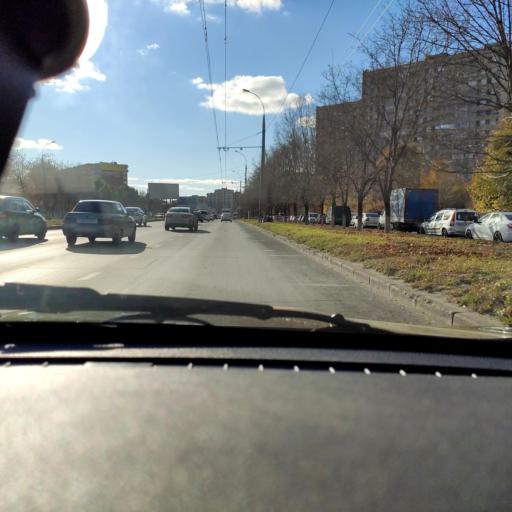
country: RU
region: Samara
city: Tol'yatti
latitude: 53.5216
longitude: 49.3194
